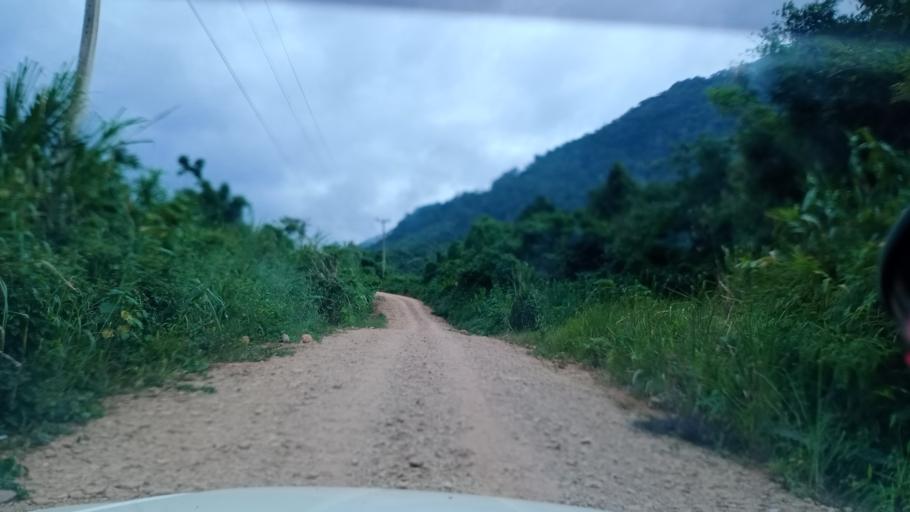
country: TH
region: Changwat Bueng Kan
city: Pak Khat
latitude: 18.7256
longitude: 103.2673
